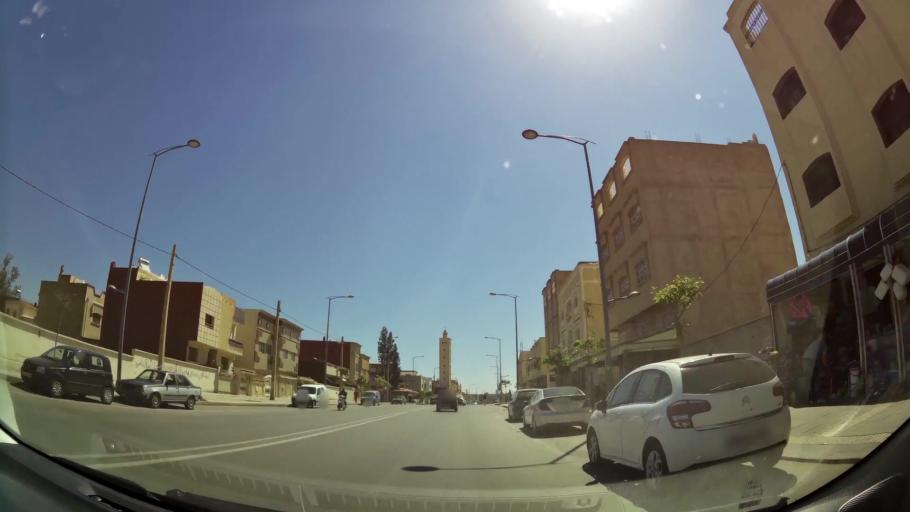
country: MA
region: Oriental
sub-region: Oujda-Angad
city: Oujda
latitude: 34.6655
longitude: -1.8881
